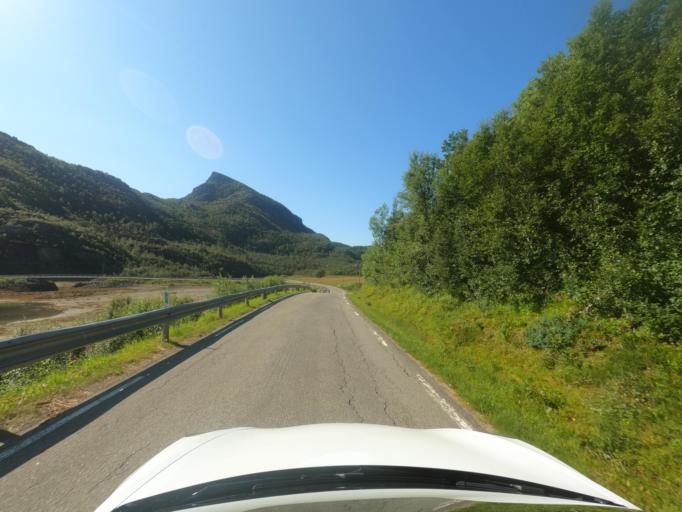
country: NO
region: Nordland
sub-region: Hadsel
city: Stokmarknes
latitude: 68.3010
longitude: 15.0402
